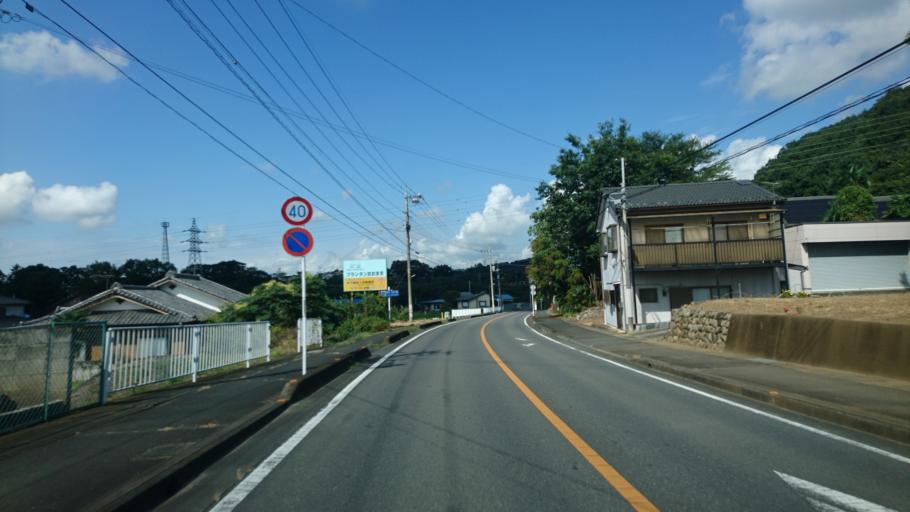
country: JP
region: Gunma
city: Omamacho-omama
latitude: 36.4342
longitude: 139.2842
